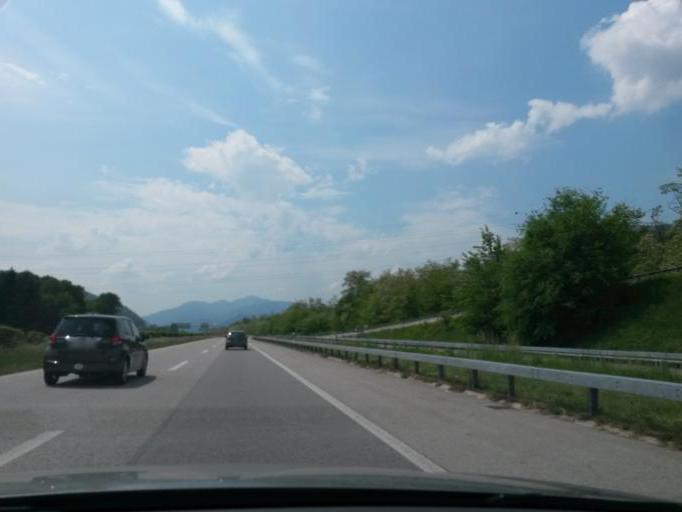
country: CH
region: Ticino
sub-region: Lugano District
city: Cadempino
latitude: 46.0279
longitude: 8.9246
